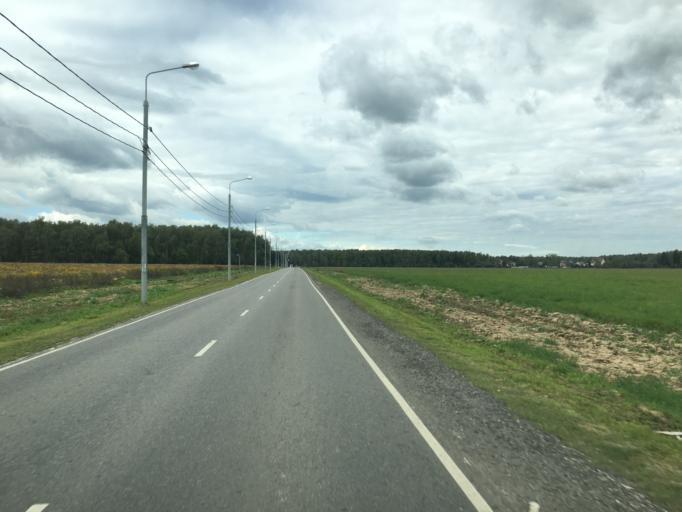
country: RU
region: Moskovskaya
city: Vatutinki
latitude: 55.4940
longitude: 37.3961
